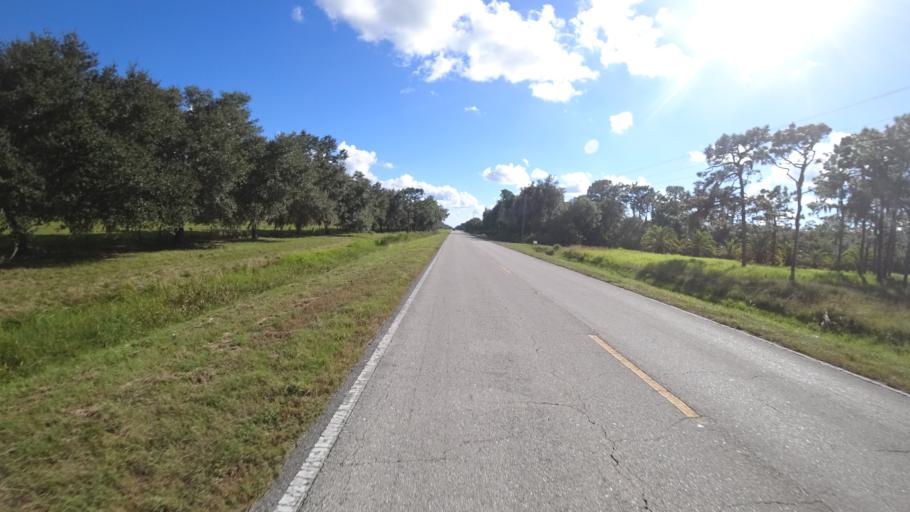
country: US
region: Florida
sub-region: Sarasota County
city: The Meadows
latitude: 27.4241
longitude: -82.3036
